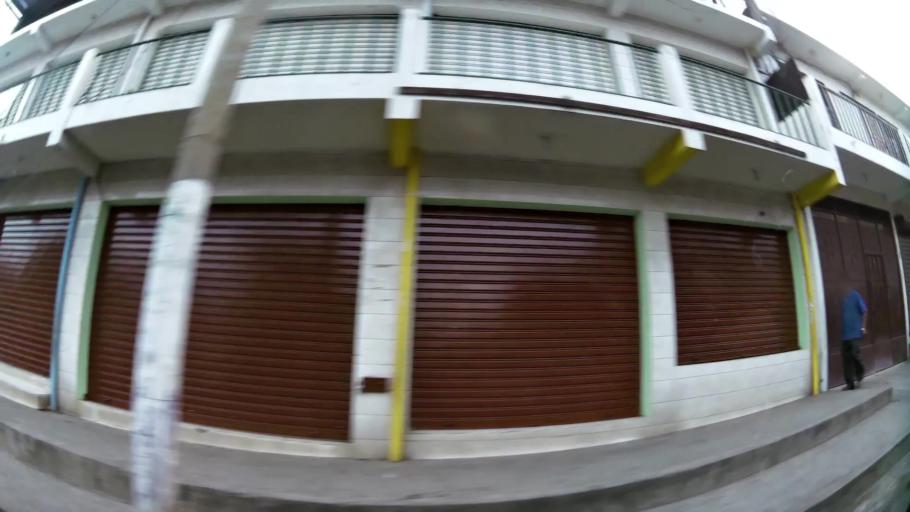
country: SV
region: San Vicente
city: San Vicente
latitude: 13.6423
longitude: -88.7859
